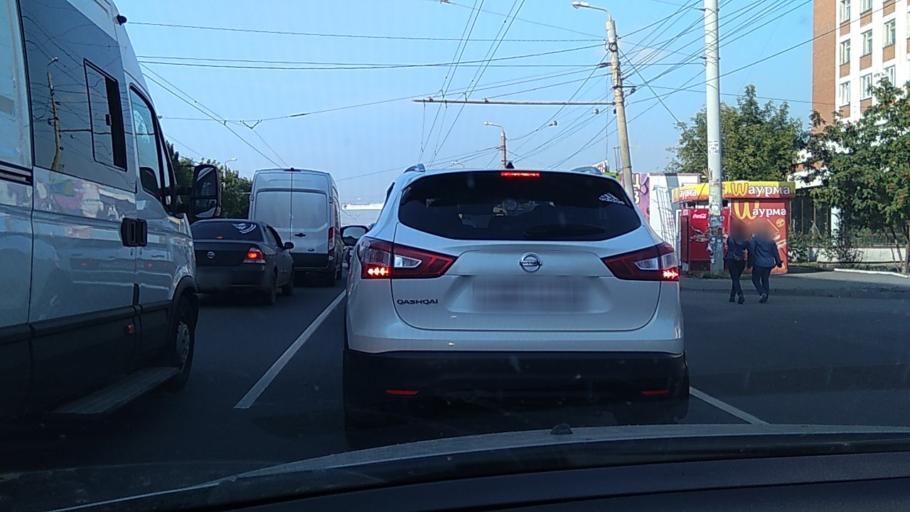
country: RU
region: Chelyabinsk
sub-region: Gorod Chelyabinsk
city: Chelyabinsk
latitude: 55.1538
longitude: 61.3895
